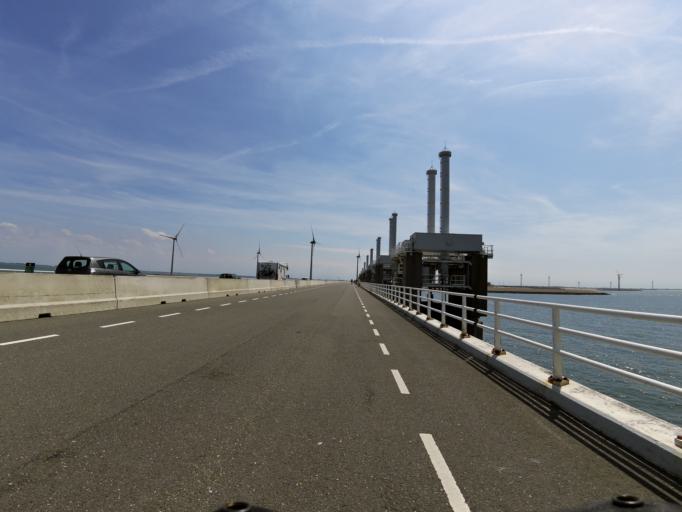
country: NL
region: Zeeland
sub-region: Schouwen-Duiveland
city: Burgh
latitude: 51.6601
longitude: 3.7227
